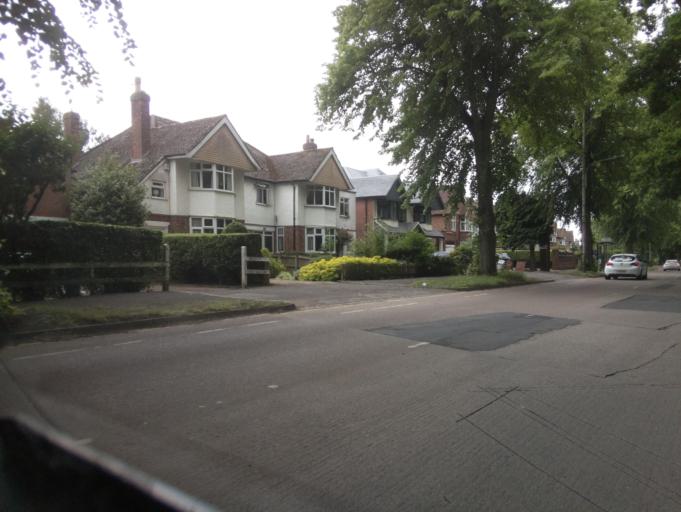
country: GB
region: England
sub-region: Leicestershire
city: Oadby
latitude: 52.6255
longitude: -1.0687
